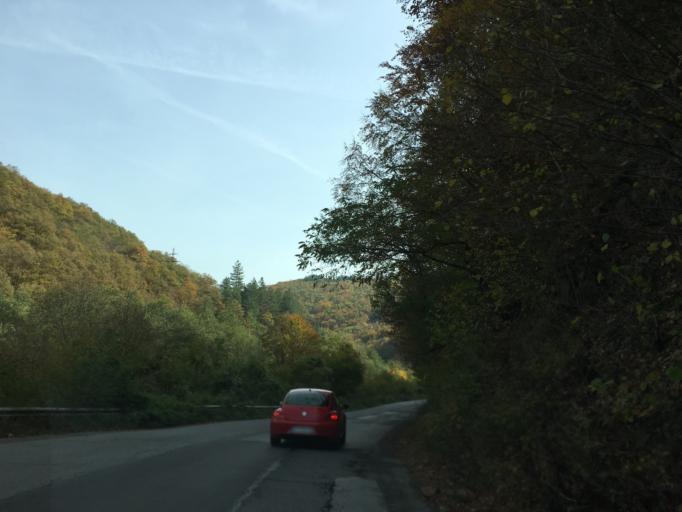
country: BG
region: Sofiya
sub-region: Obshtina Elin Pelin
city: Elin Pelin
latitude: 42.5508
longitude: 23.4672
